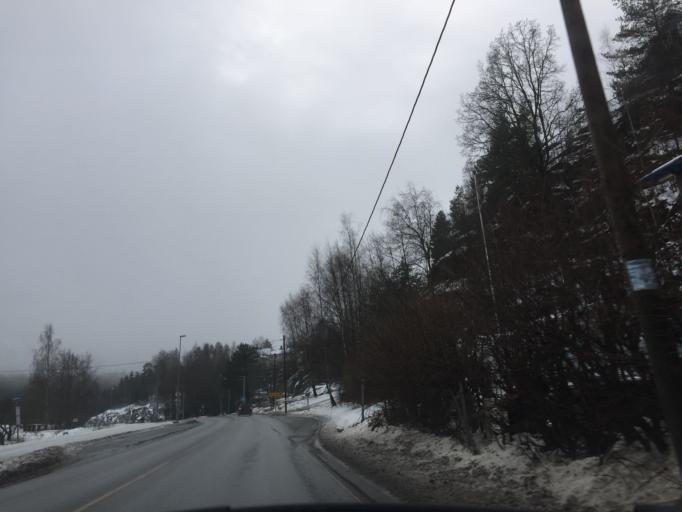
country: NO
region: Akershus
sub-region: Frogn
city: Drobak
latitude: 59.6686
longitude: 10.6597
